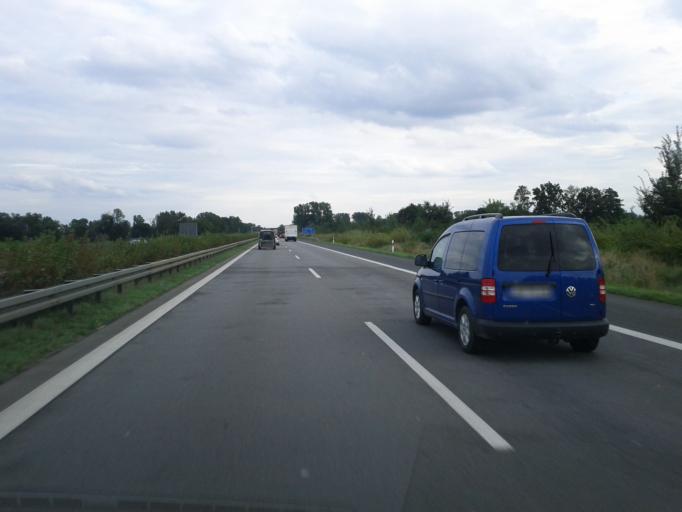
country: DE
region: Brandenburg
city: Mittenwalde
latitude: 52.2882
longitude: 13.5621
